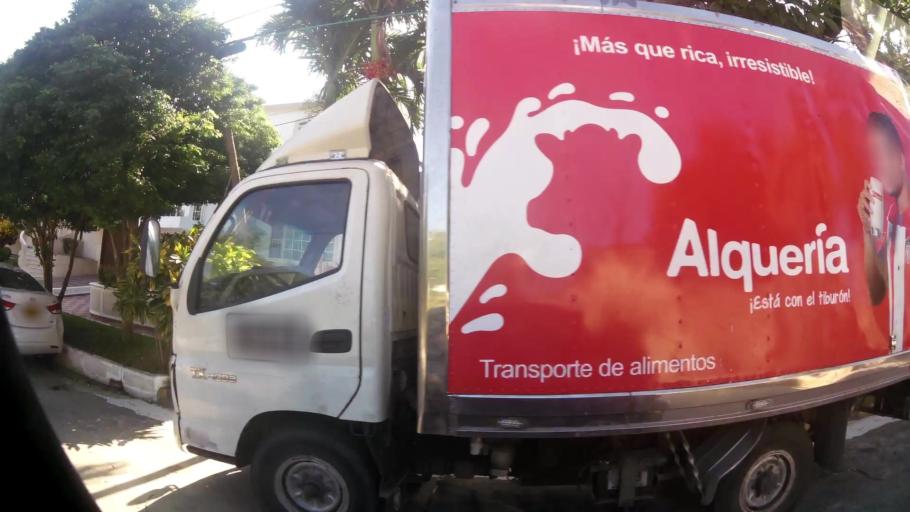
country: CO
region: Atlantico
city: Barranquilla
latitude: 10.9969
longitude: -74.8262
